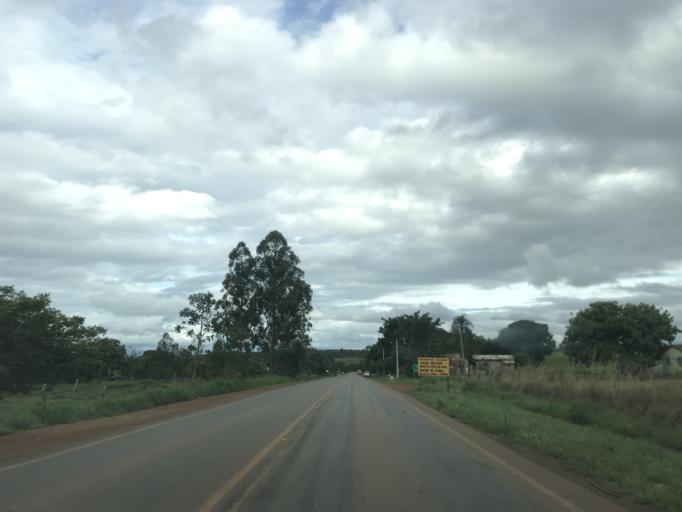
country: BR
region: Goias
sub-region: Vianopolis
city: Vianopolis
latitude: -16.7256
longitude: -48.4365
